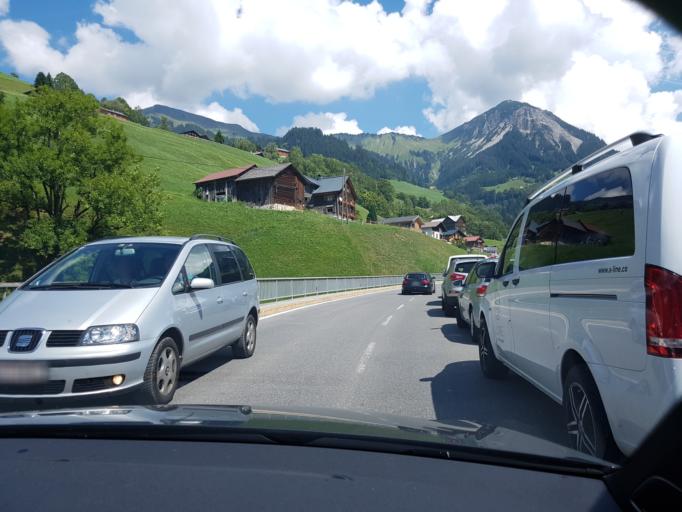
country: AT
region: Vorarlberg
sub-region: Politischer Bezirk Bregenz
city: Damuels
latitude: 47.2410
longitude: 9.9078
